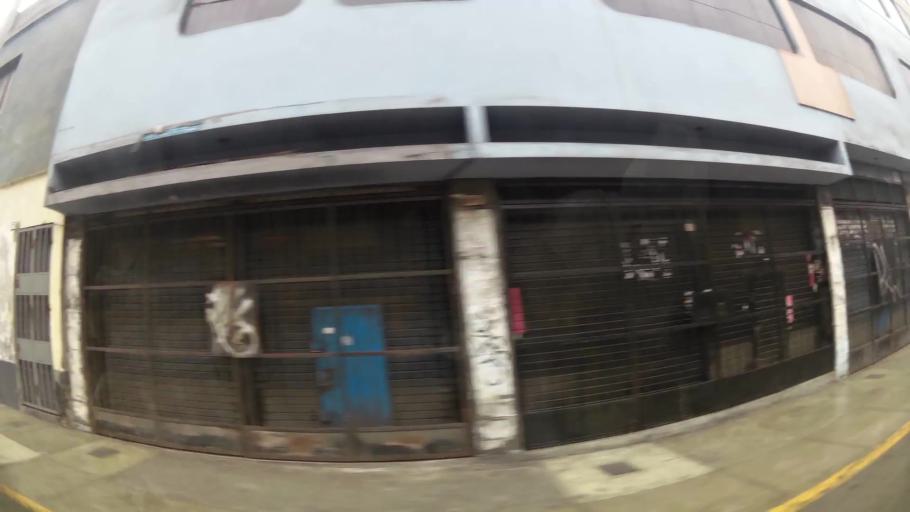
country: PE
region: Lima
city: Lima
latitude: -12.0739
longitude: -77.0311
